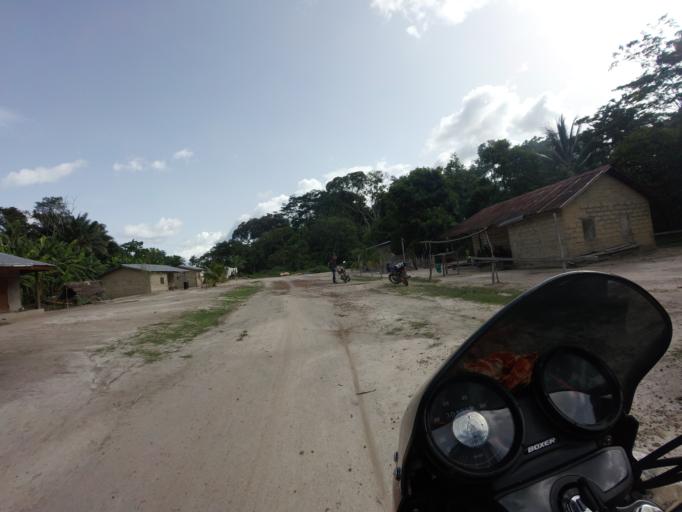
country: SL
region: Eastern Province
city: Tombu
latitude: 8.4876
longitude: -10.7700
